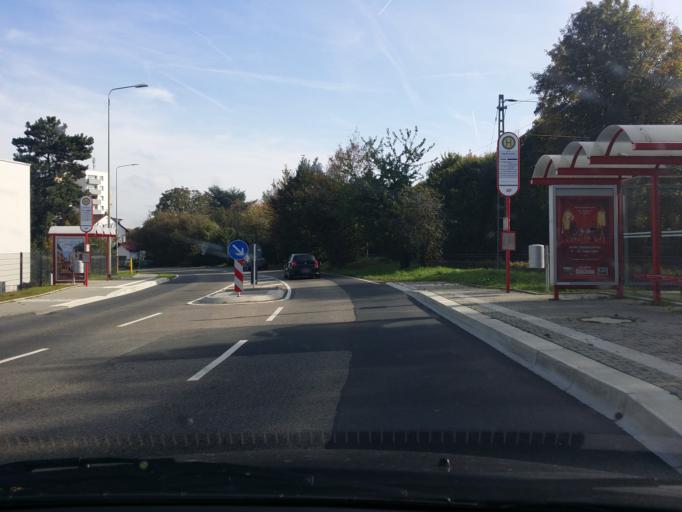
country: DE
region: Hesse
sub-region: Regierungsbezirk Darmstadt
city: Kriftel
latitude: 50.0795
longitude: 8.4619
